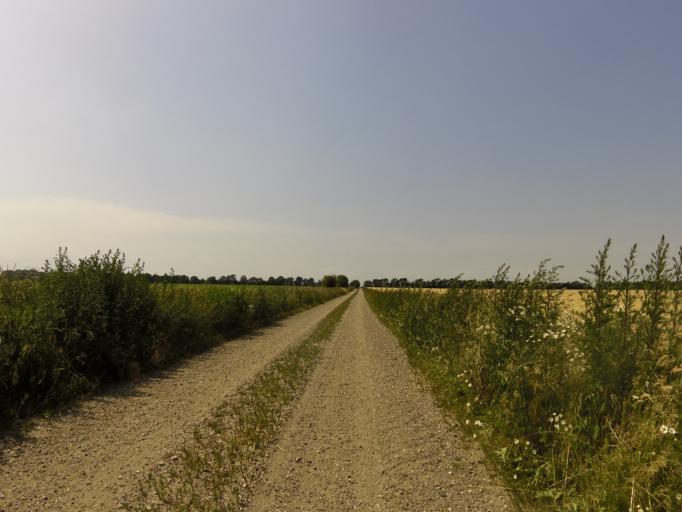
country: DK
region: South Denmark
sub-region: Aabenraa Kommune
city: Rodekro
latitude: 55.1416
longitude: 9.2196
